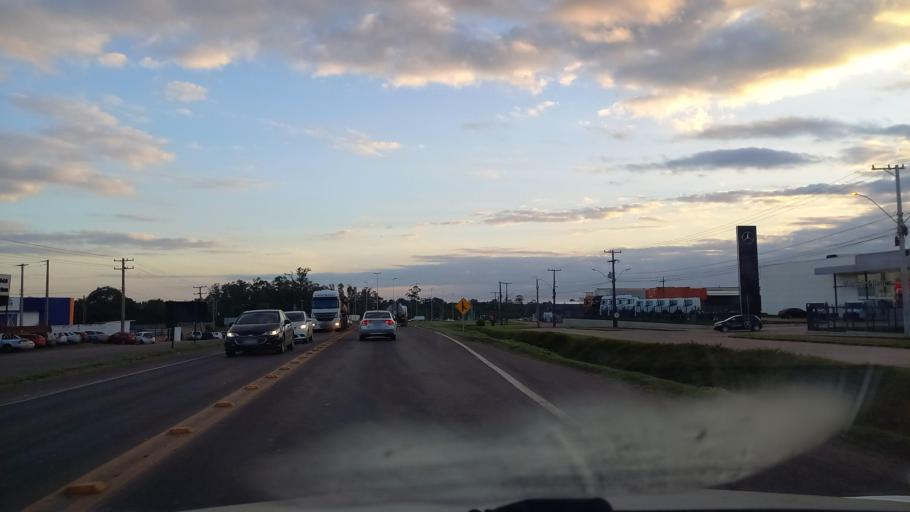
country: BR
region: Rio Grande do Sul
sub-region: Santa Cruz Do Sul
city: Santa Cruz do Sul
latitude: -29.6878
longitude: -52.4472
